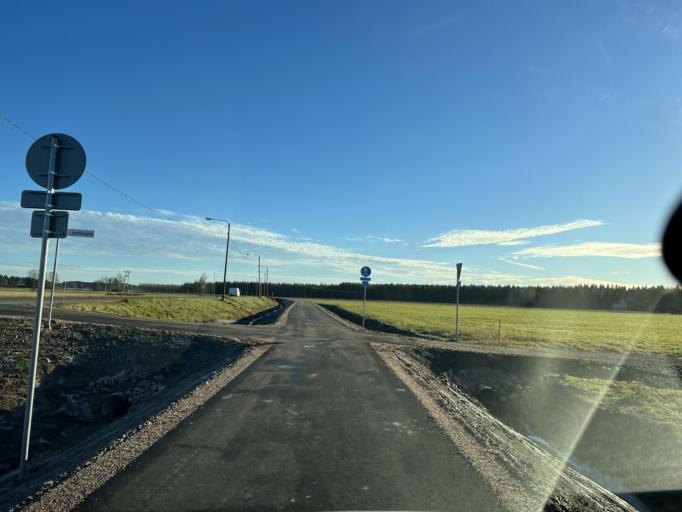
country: FI
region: Northern Ostrobothnia
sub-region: Nivala-Haapajaervi
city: Nivala
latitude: 63.9526
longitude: 24.8737
